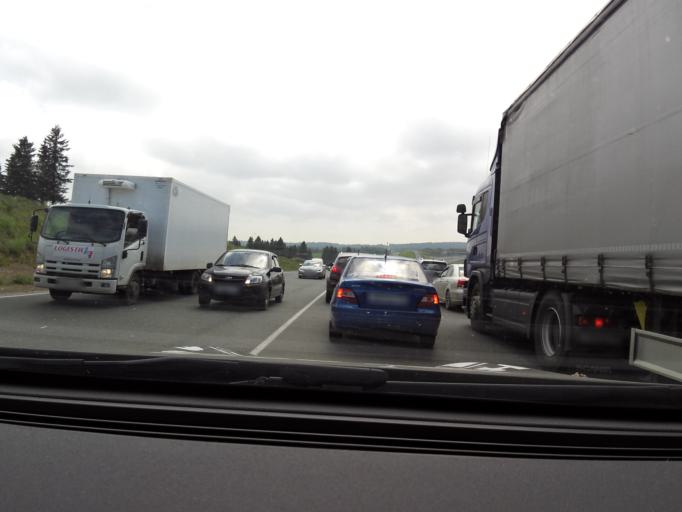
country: RU
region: Perm
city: Zvezdnyy
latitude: 57.7893
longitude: 56.3384
